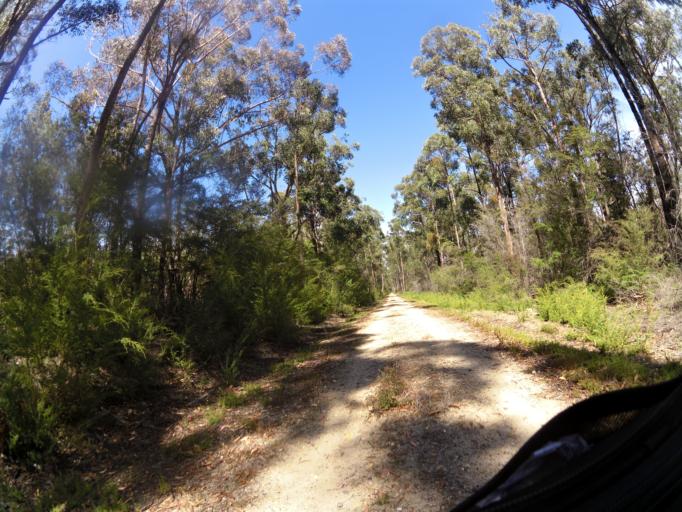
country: AU
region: Victoria
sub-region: East Gippsland
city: Lakes Entrance
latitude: -37.7195
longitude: 148.1218
